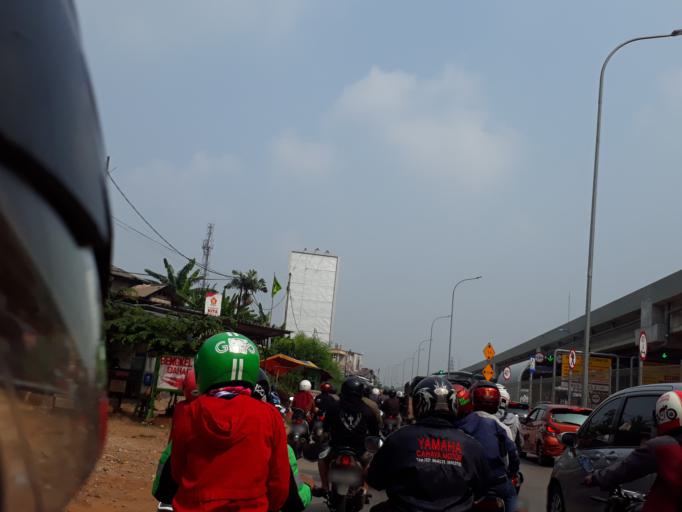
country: ID
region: West Java
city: Bekasi
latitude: -6.2498
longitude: 106.9643
